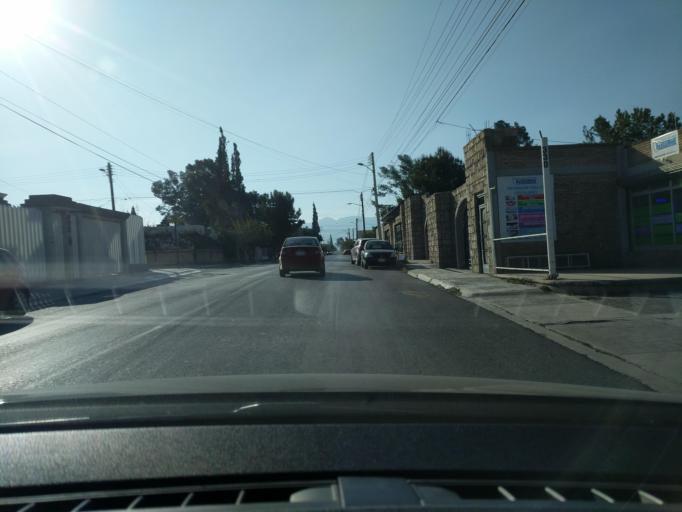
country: MX
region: Coahuila
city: Saltillo
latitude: 25.4627
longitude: -100.9849
